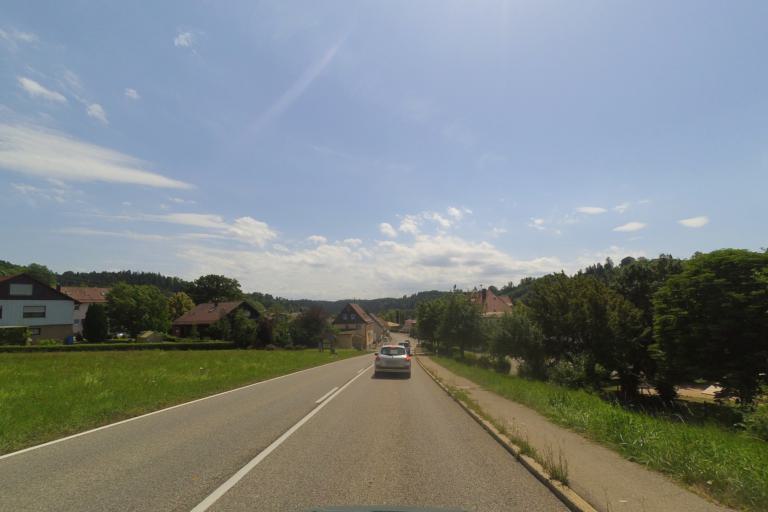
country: DE
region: Baden-Wuerttemberg
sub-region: Regierungsbezirk Stuttgart
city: Eschach
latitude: 48.9461
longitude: 9.8572
